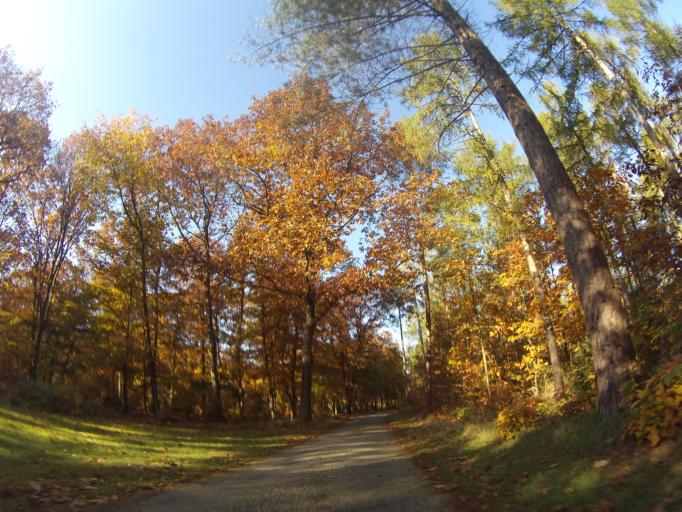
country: NL
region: Utrecht
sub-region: Gemeente Utrechtse Heuvelrug
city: Driebergen-Rijsenburg
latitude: 52.0868
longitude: 5.3167
